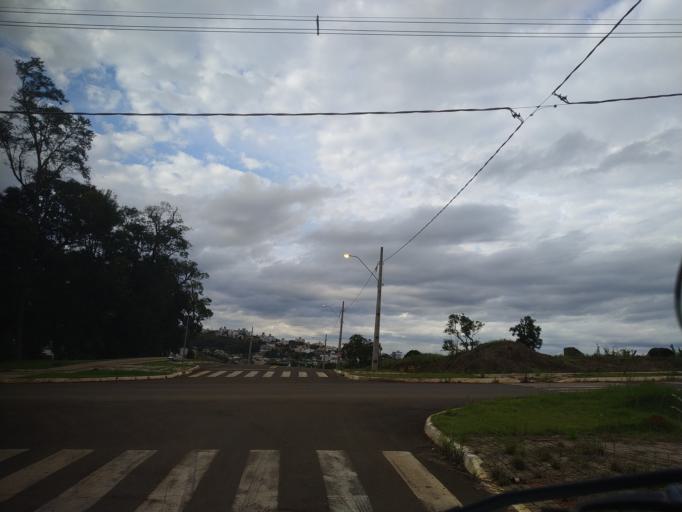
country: BR
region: Santa Catarina
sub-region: Chapeco
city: Chapeco
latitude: -27.0646
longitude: -52.6221
